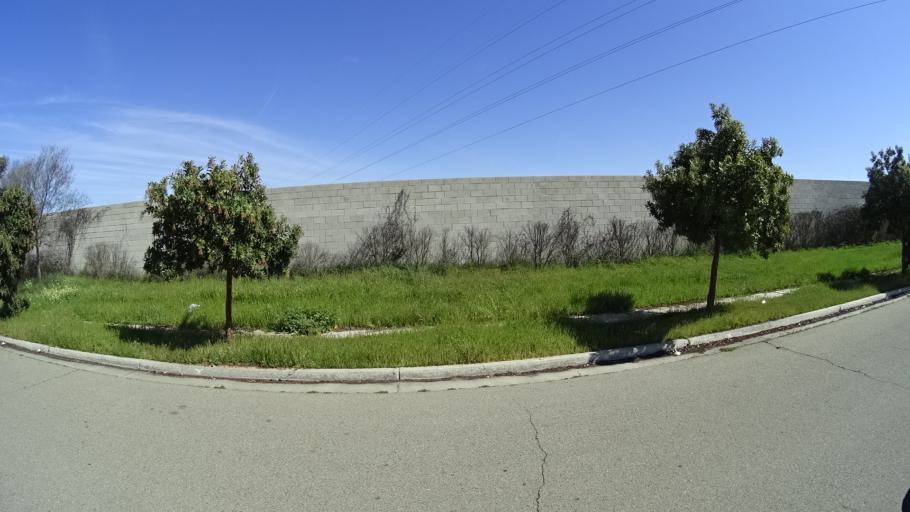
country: US
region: California
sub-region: Fresno County
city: Biola
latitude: 36.8174
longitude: -119.9013
